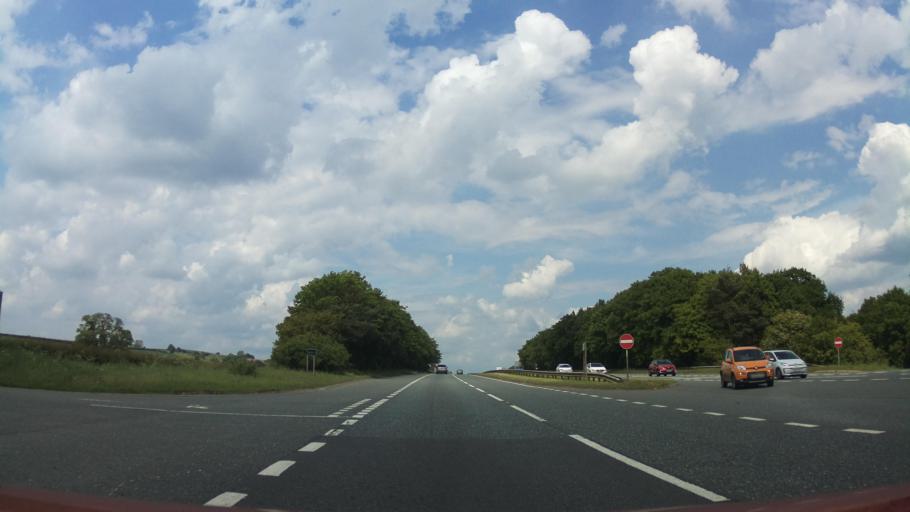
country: GB
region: England
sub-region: North Yorkshire
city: Thirsk
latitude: 54.3126
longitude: -1.3387
